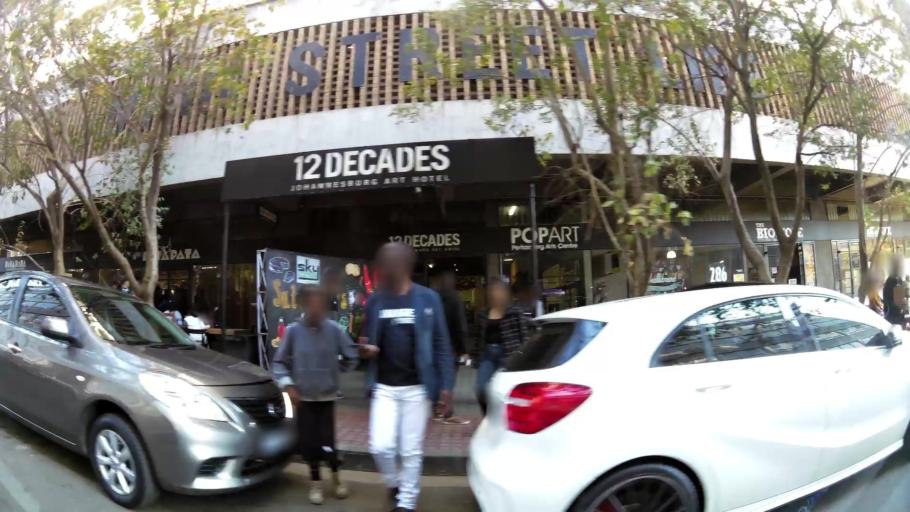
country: ZA
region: Gauteng
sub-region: City of Johannesburg Metropolitan Municipality
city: Johannesburg
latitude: -26.2041
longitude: 28.0596
